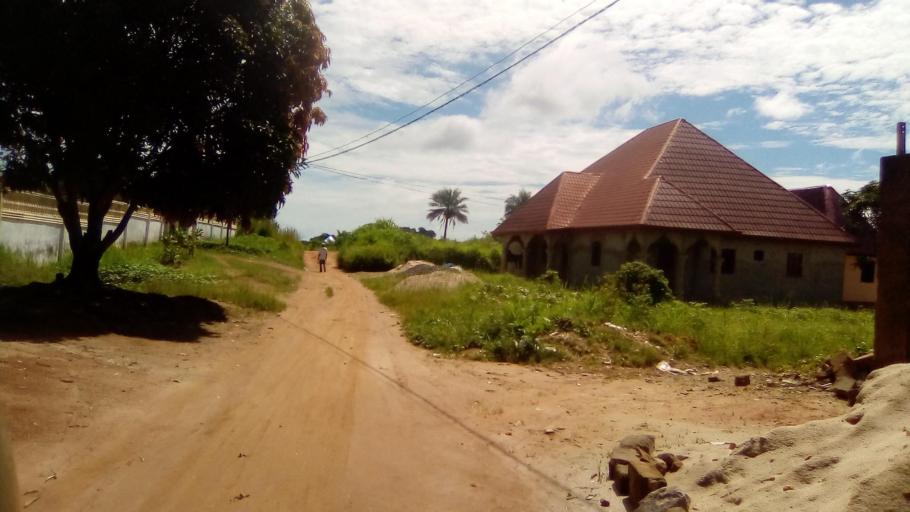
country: SL
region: Eastern Province
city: Koidu
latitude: 8.6393
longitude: -10.9953
